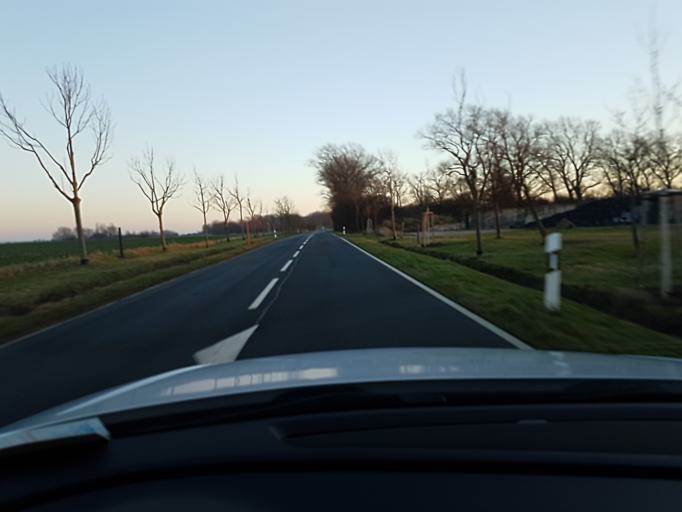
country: DE
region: Mecklenburg-Vorpommern
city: Wiek
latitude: 54.6039
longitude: 13.2877
